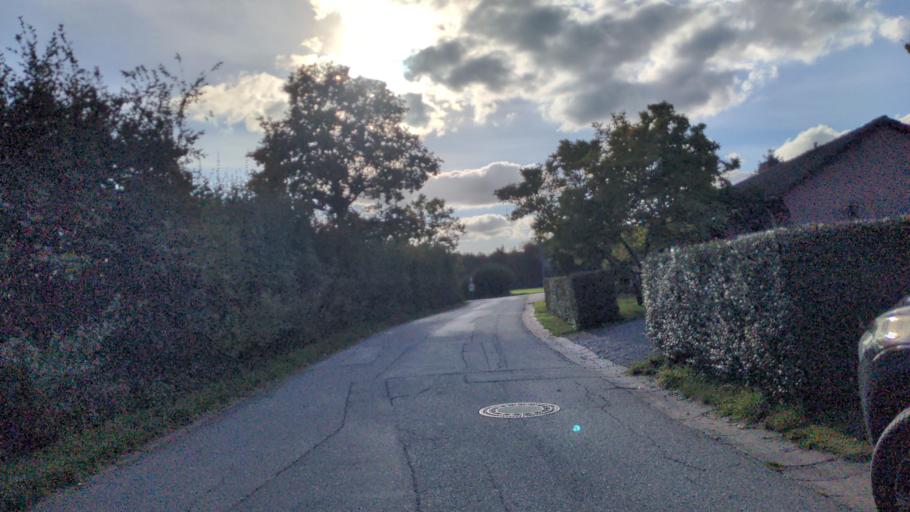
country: DE
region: Schleswig-Holstein
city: Manhagen
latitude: 54.1946
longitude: 10.9133
